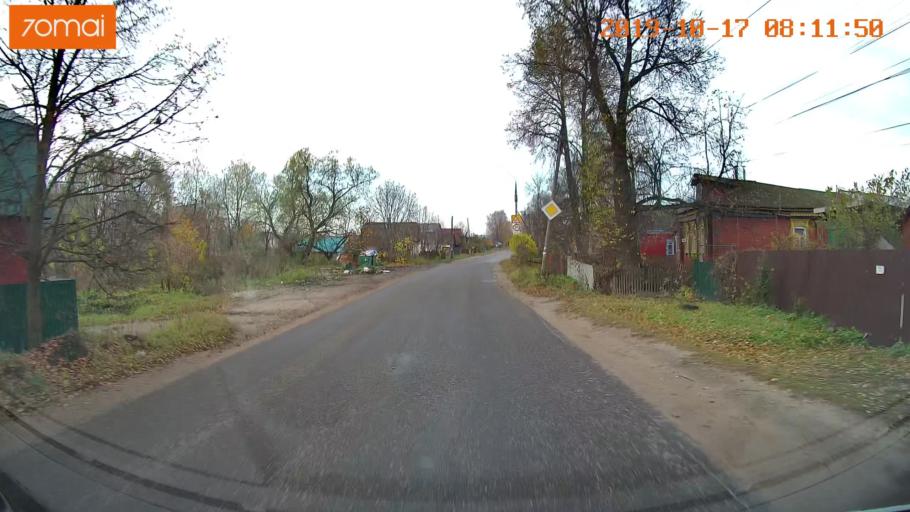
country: RU
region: Vladimir
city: Kol'chugino
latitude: 56.3011
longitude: 39.3646
